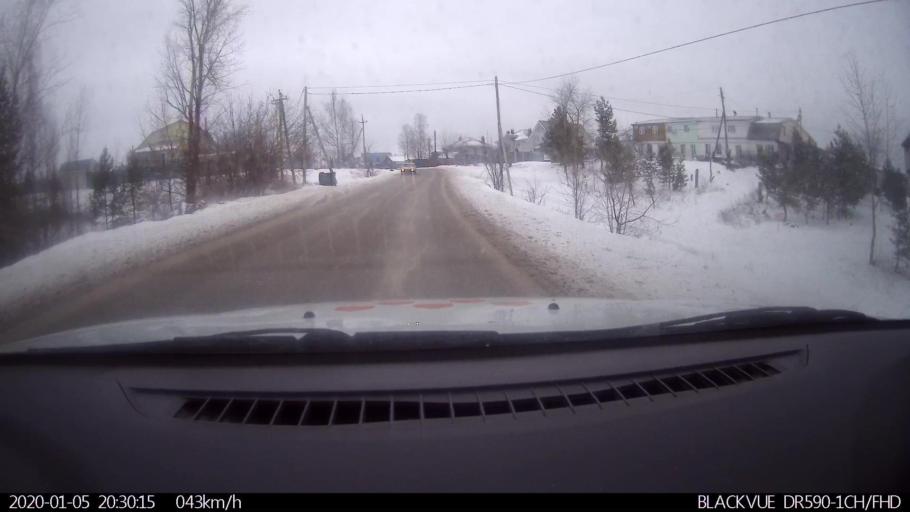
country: RU
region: Nizjnij Novgorod
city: Lukino
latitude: 56.3974
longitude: 43.7296
